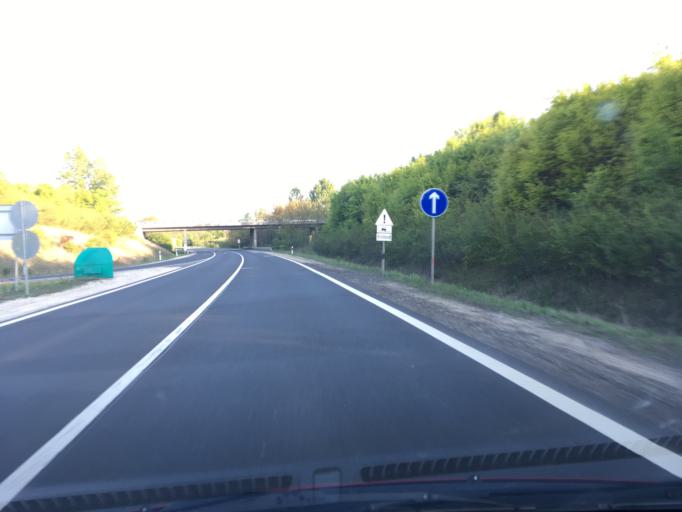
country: HU
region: Pest
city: Vac
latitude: 47.7944
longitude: 19.1531
